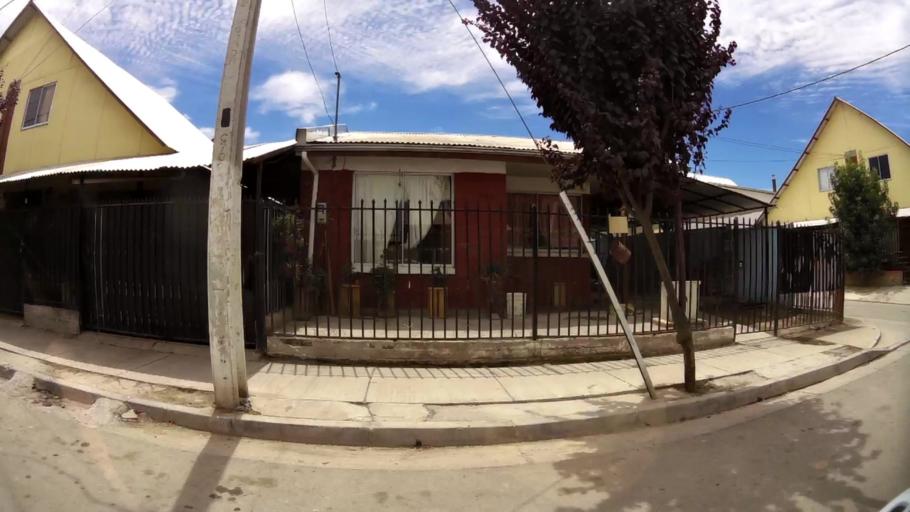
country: CL
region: O'Higgins
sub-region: Provincia de Cachapoal
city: Graneros
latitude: -34.0723
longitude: -70.7371
